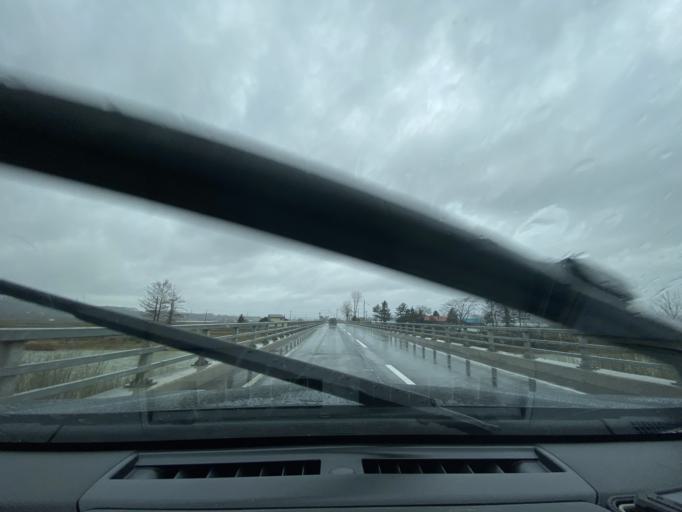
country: JP
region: Hokkaido
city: Fukagawa
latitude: 43.8092
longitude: 142.0149
